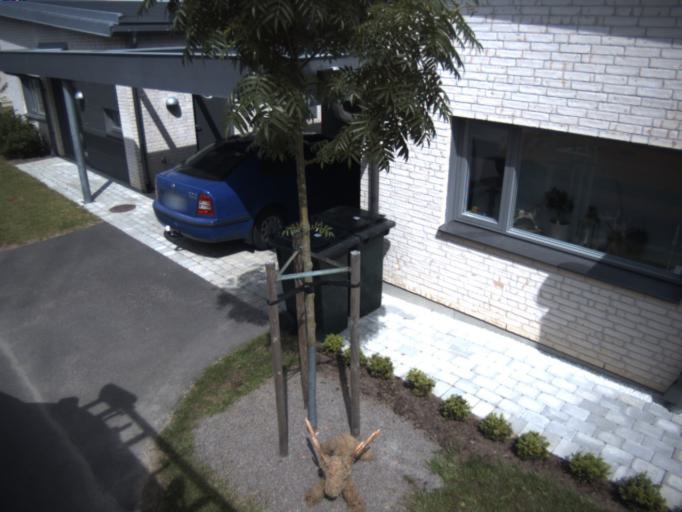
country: SE
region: Skane
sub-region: Helsingborg
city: Helsingborg
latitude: 56.0970
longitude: 12.6631
